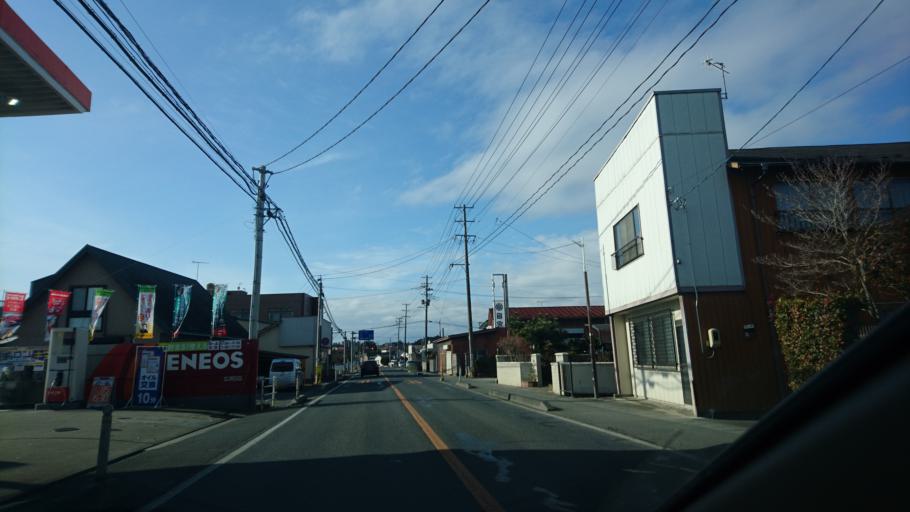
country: JP
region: Miyagi
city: Yamoto
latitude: 38.4723
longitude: 141.2147
